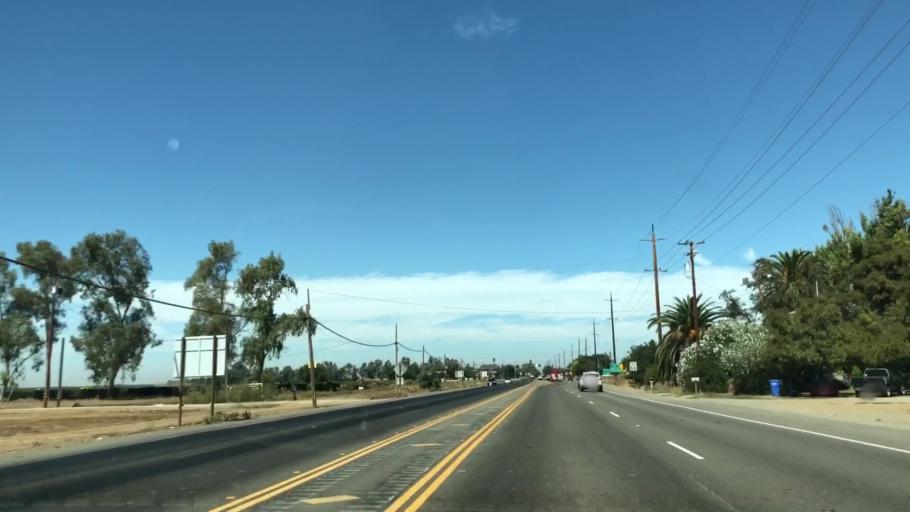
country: US
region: California
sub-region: Contra Costa County
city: Byron
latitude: 37.8924
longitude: -121.6413
